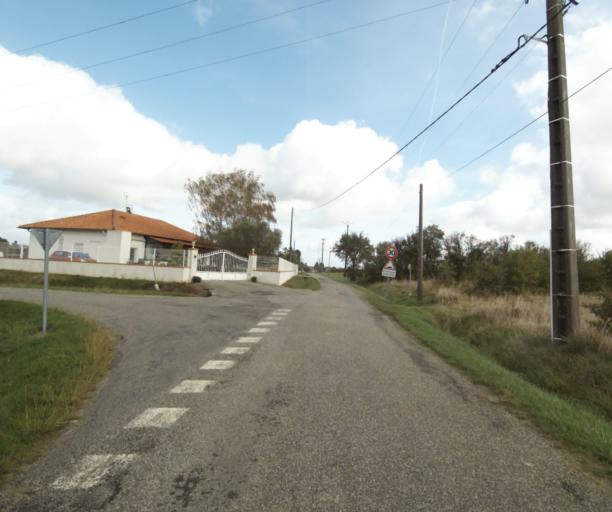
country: FR
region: Midi-Pyrenees
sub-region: Departement du Tarn-et-Garonne
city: Finhan
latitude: 43.8958
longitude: 1.1310
